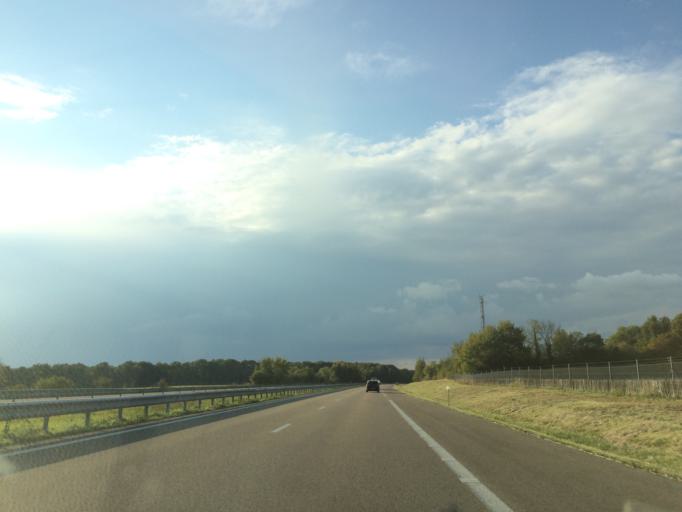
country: FR
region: Bourgogne
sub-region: Departement de l'Yonne
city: Cheroy
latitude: 48.1148
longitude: 2.9880
